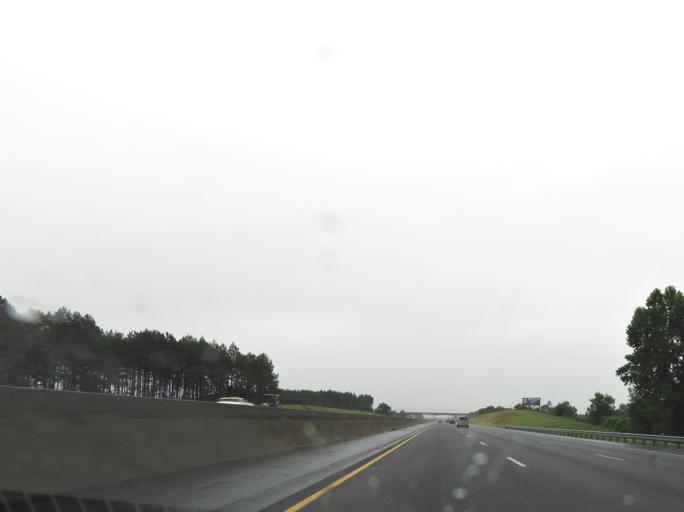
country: US
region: Georgia
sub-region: Tift County
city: Tifton
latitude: 31.5355
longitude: -83.5266
